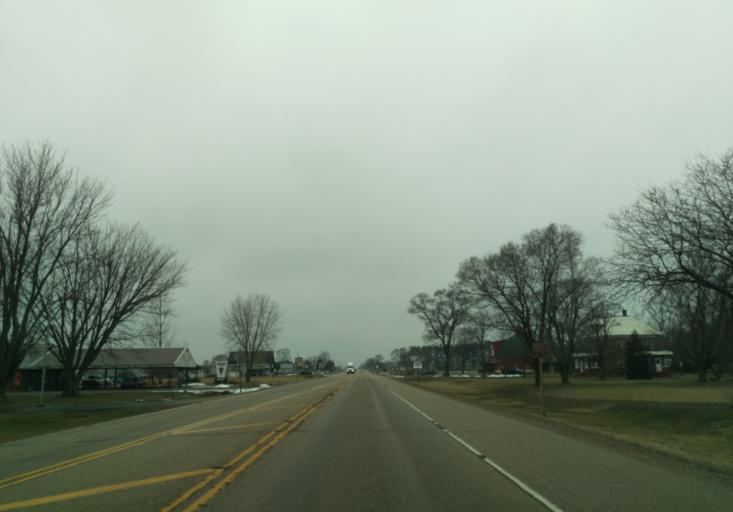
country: US
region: Wisconsin
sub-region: Sauk County
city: Spring Green
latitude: 43.1897
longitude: -90.0754
